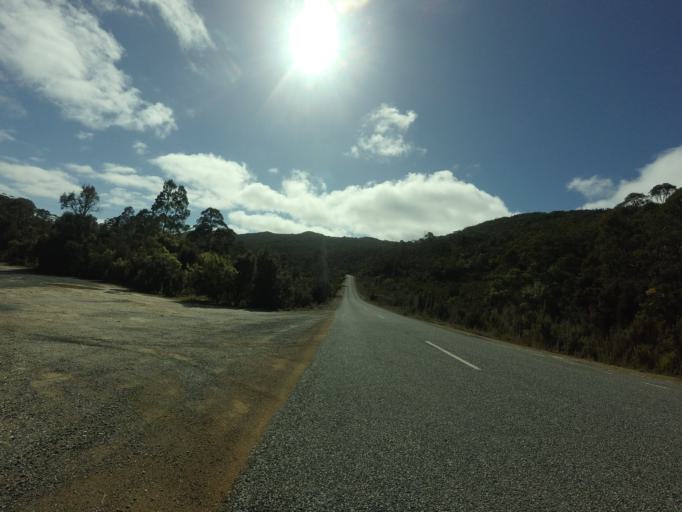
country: AU
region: Tasmania
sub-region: Huon Valley
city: Geeveston
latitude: -42.8153
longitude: 146.3861
